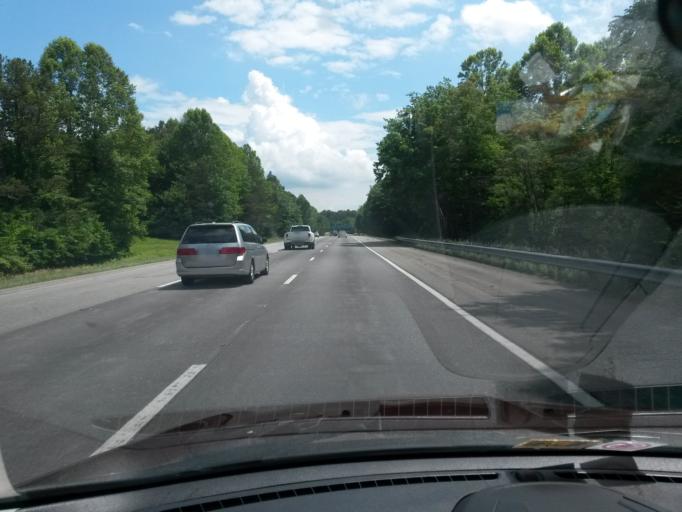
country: US
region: North Carolina
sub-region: Surry County
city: Dobson
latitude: 36.5019
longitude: -80.7424
